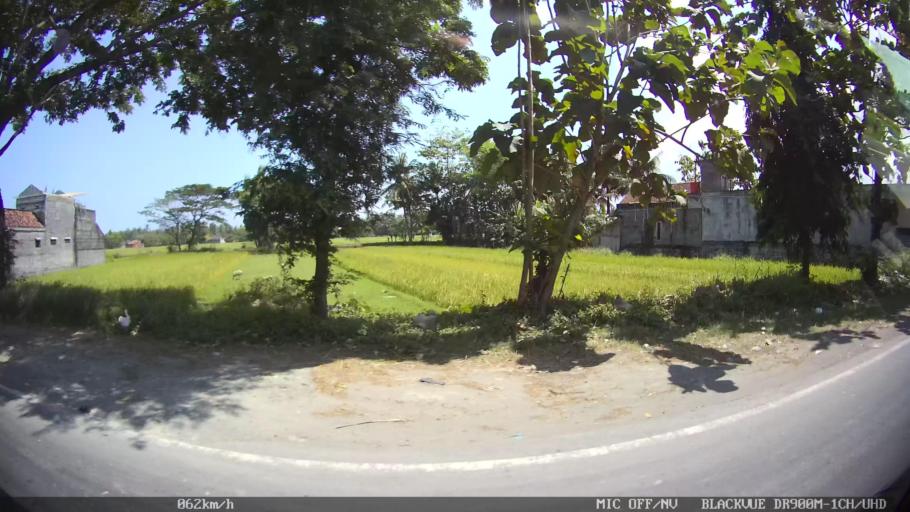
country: ID
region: Daerah Istimewa Yogyakarta
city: Pandak
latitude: -7.9229
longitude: 110.2805
